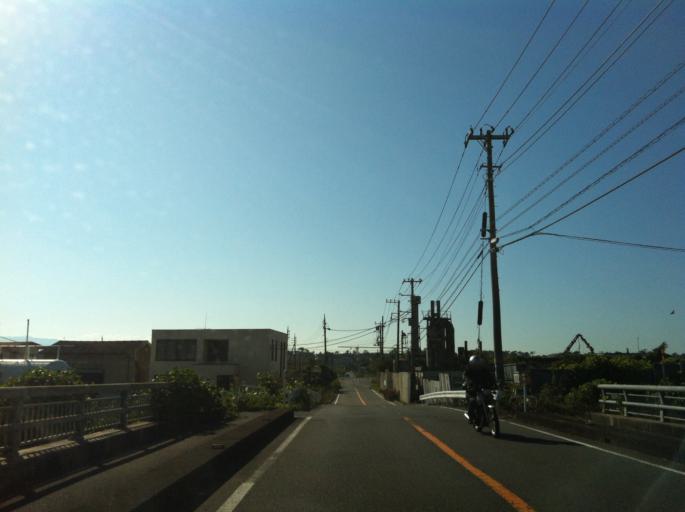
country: JP
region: Shizuoka
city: Fuji
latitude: 35.1361
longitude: 138.7755
